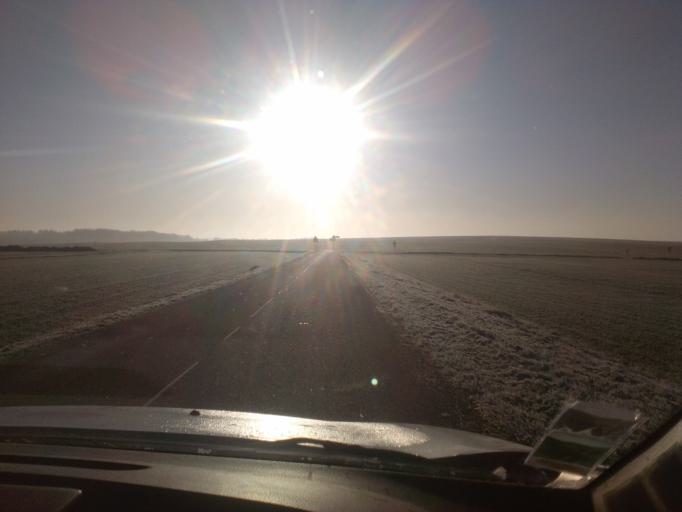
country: FR
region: Lorraine
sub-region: Departement des Vosges
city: Darnieulles
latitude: 48.1933
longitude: 6.2292
